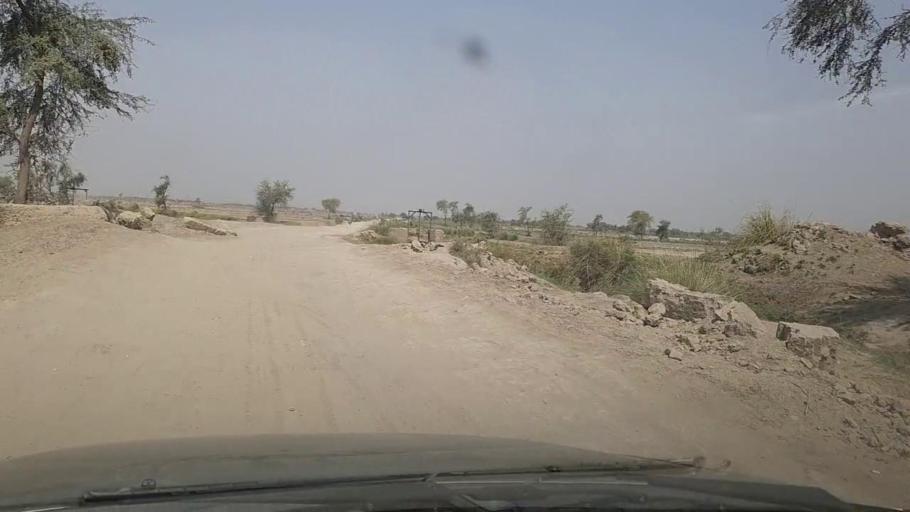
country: PK
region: Sindh
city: Thul
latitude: 28.4036
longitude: 68.7047
